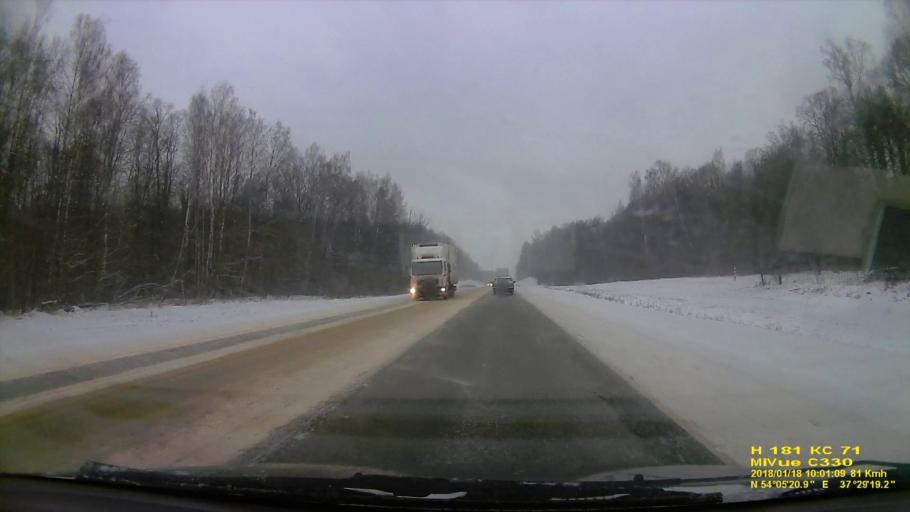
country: RU
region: Tula
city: Pervomayskiy
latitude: 54.0892
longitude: 37.4887
